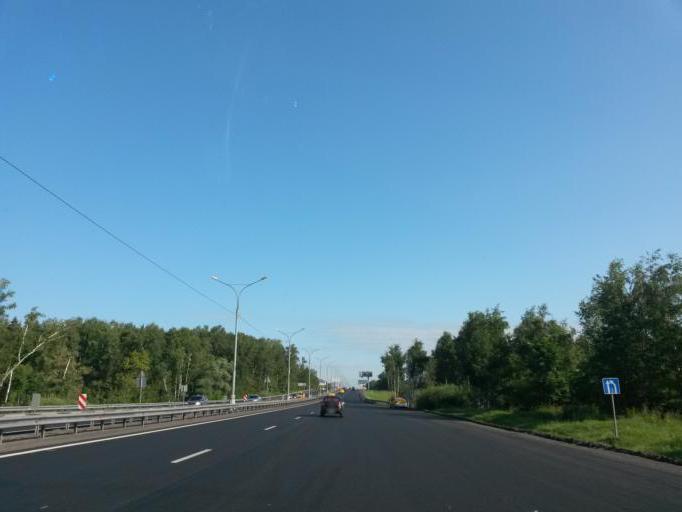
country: RU
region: Moskovskaya
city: Gorki-Leninskiye
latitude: 55.5147
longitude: 37.8283
